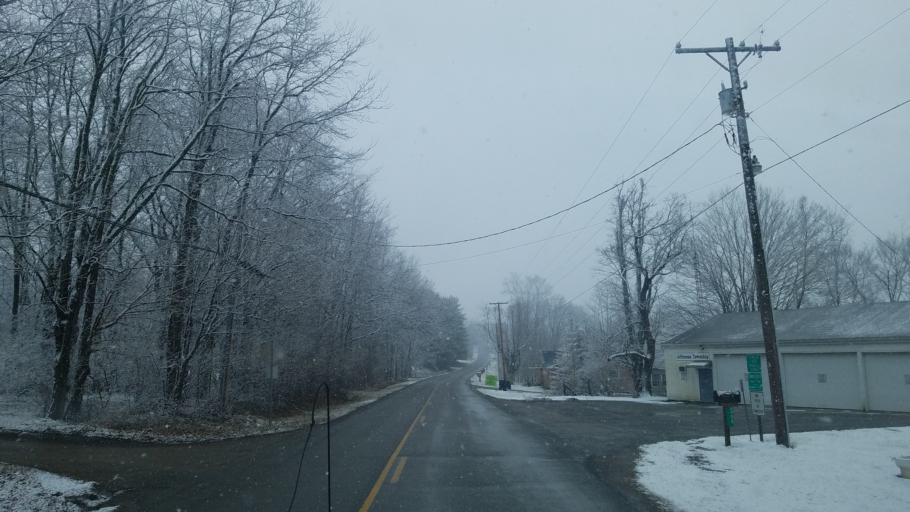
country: US
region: Ohio
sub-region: Logan County
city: Bellefontaine
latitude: 40.3335
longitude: -83.6712
